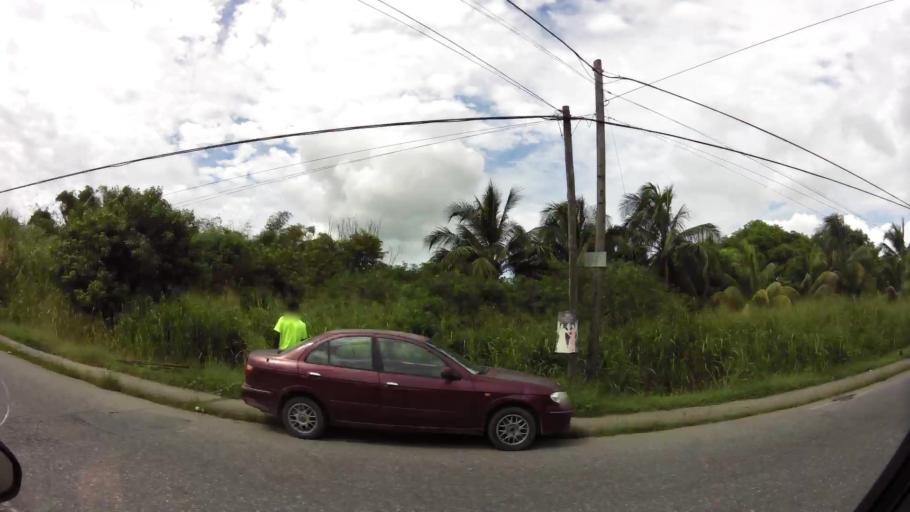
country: TT
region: Couva-Tabaquite-Talparo
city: Couva
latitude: 10.4156
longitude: -61.4707
